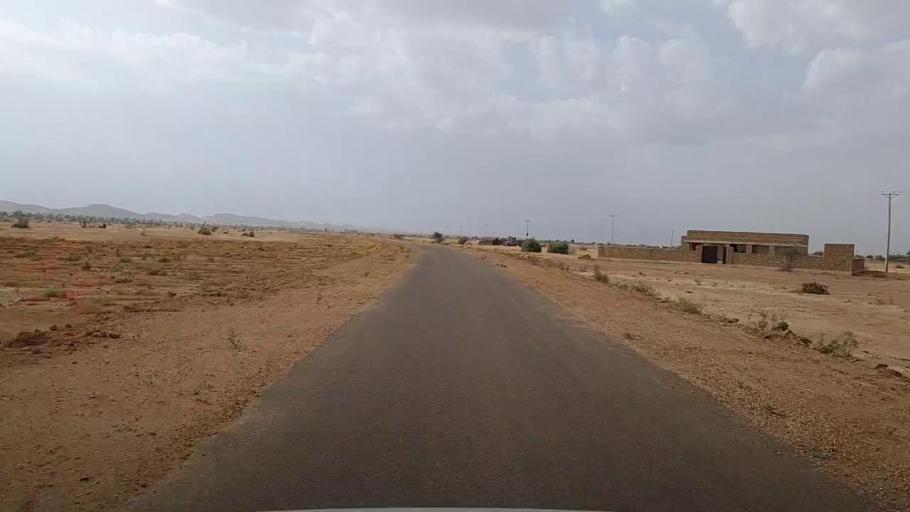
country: PK
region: Sindh
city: Jamshoro
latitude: 25.4708
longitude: 67.6761
